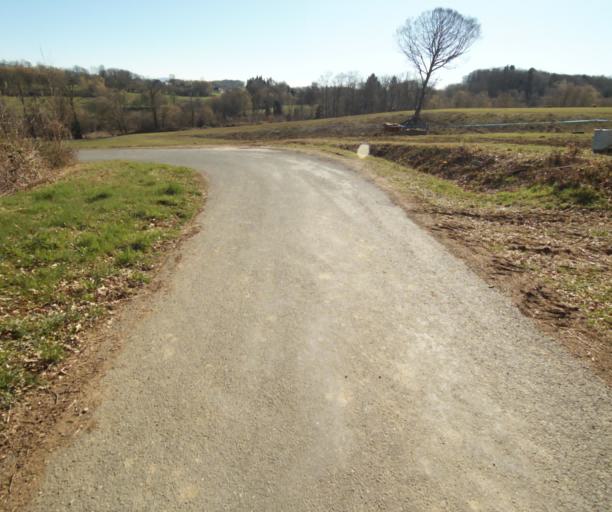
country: FR
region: Limousin
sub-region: Departement de la Correze
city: Seilhac
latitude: 45.3952
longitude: 1.7002
